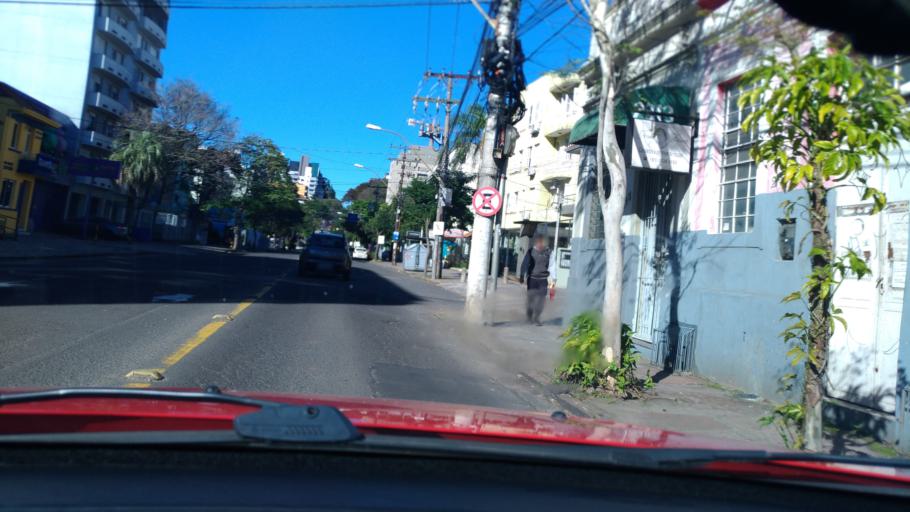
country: BR
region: Rio Grande do Sul
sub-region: Porto Alegre
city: Porto Alegre
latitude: -30.0179
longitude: -51.1973
